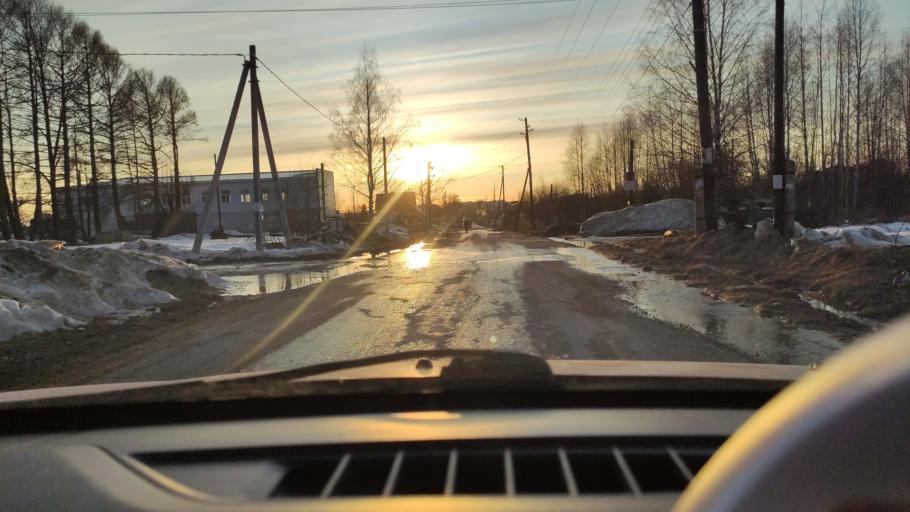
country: RU
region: Perm
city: Polazna
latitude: 58.1169
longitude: 56.4045
